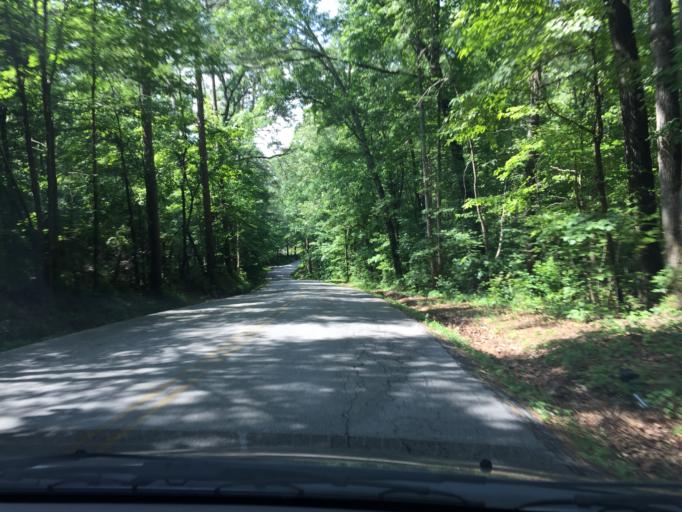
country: US
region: Tennessee
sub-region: Hamilton County
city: Collegedale
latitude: 35.0608
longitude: -85.0478
